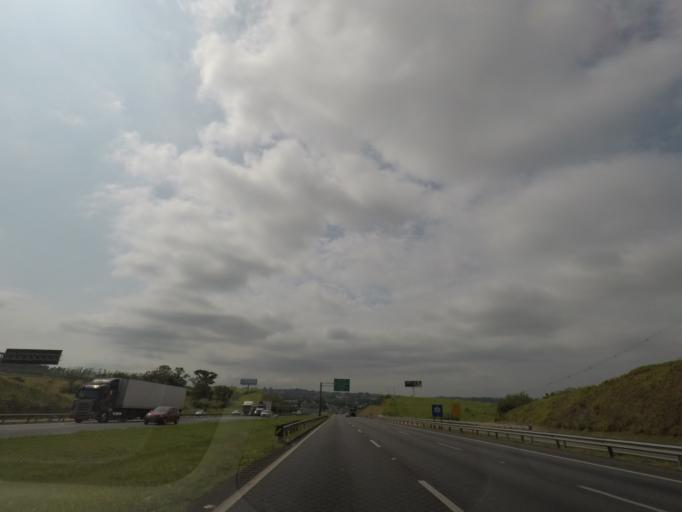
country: BR
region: Sao Paulo
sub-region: Campinas
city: Campinas
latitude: -22.8775
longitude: -47.0160
